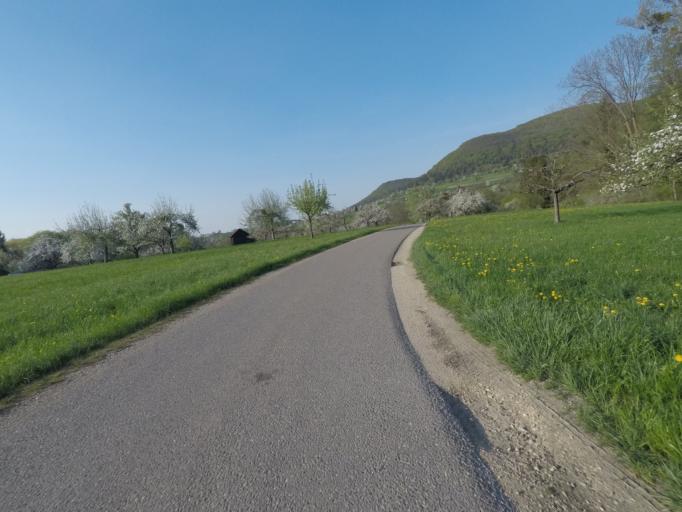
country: DE
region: Baden-Wuerttemberg
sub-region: Tuebingen Region
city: Eningen unter Achalm
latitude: 48.4695
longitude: 9.2612
